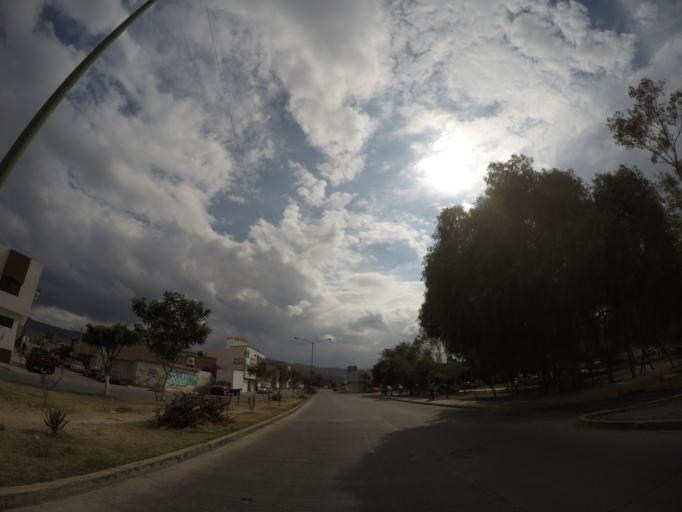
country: MX
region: San Luis Potosi
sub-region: San Luis Potosi
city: San Luis Potosi
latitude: 22.1264
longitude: -100.9789
